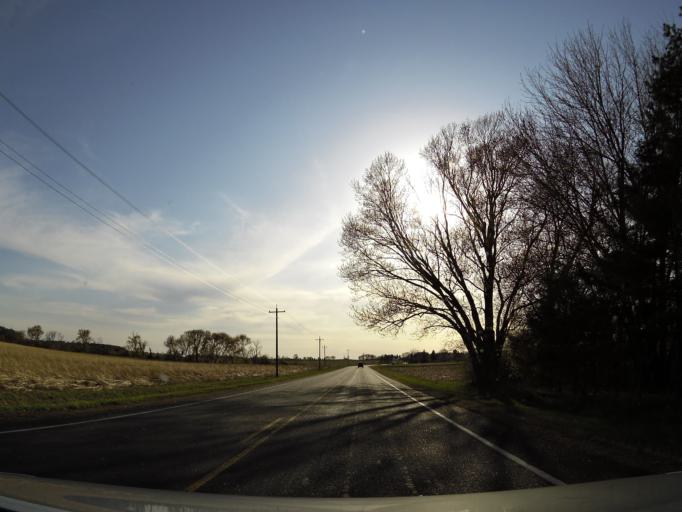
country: US
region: Wisconsin
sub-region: Pierce County
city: River Falls
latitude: 44.8250
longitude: -92.6977
